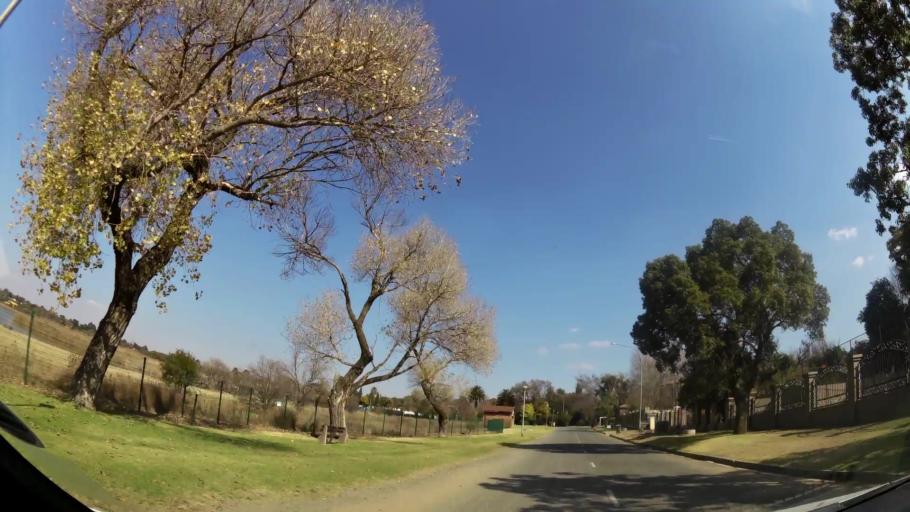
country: ZA
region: Gauteng
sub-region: Ekurhuleni Metropolitan Municipality
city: Benoni
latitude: -26.1907
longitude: 28.2909
